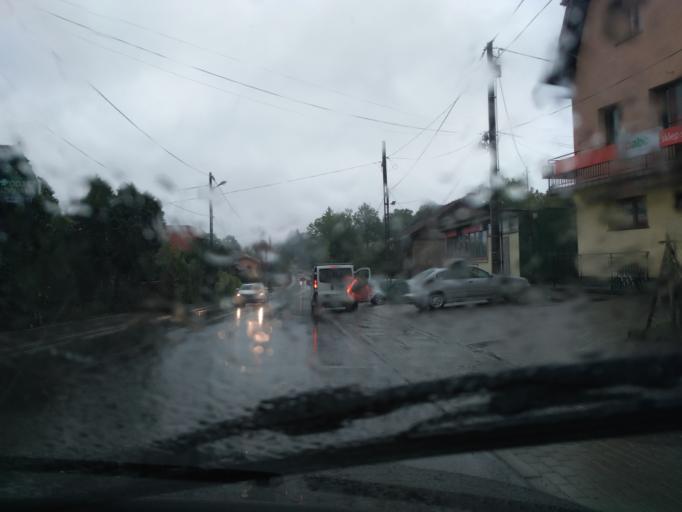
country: PL
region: Subcarpathian Voivodeship
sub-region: Powiat jasielski
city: Debowiec
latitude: 49.6808
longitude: 21.4592
